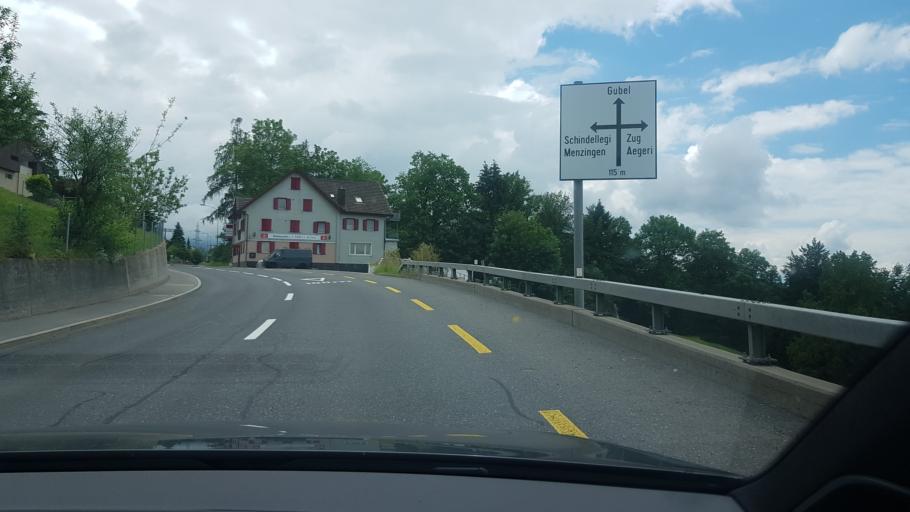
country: CH
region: Zug
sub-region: Zug
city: Menzingen
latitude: 47.1836
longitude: 8.5699
